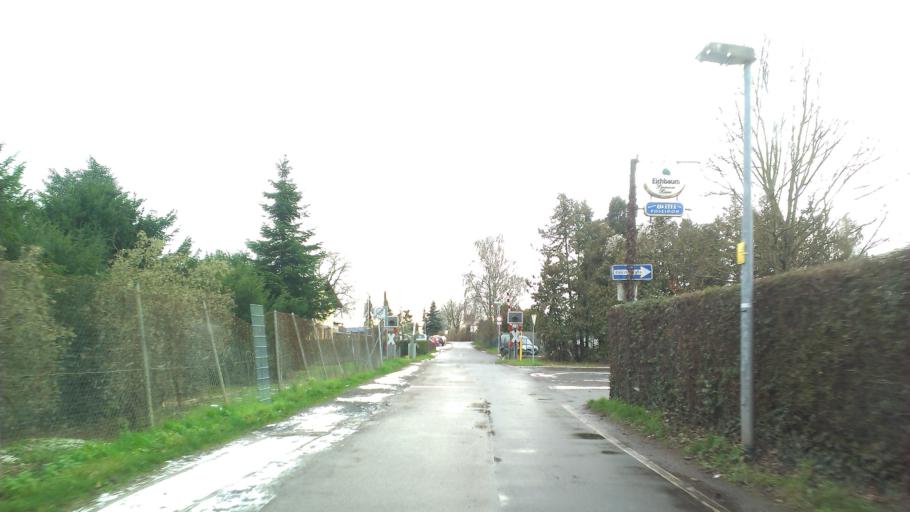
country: DE
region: Rheinland-Pfalz
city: Worms
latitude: 49.6290
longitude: 8.3396
